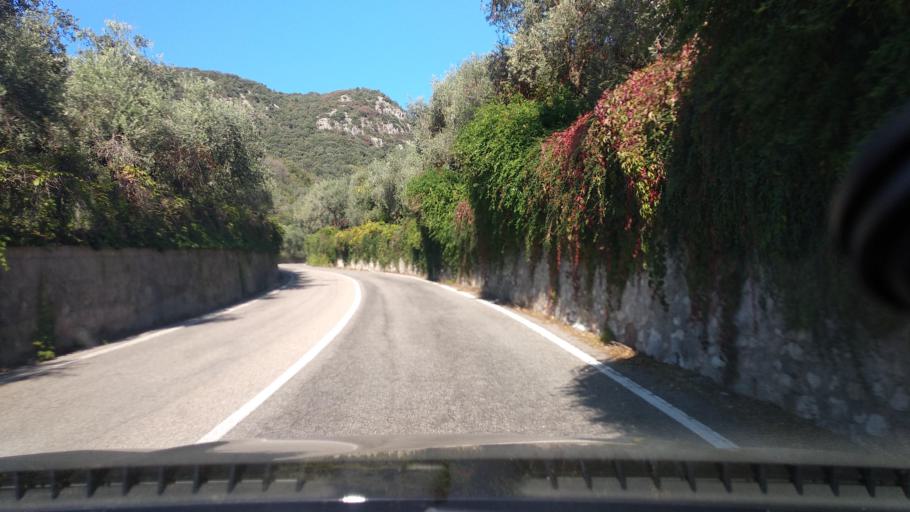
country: IT
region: Veneto
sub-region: Provincia di Verona
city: Garda
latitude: 45.5818
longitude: 10.7025
